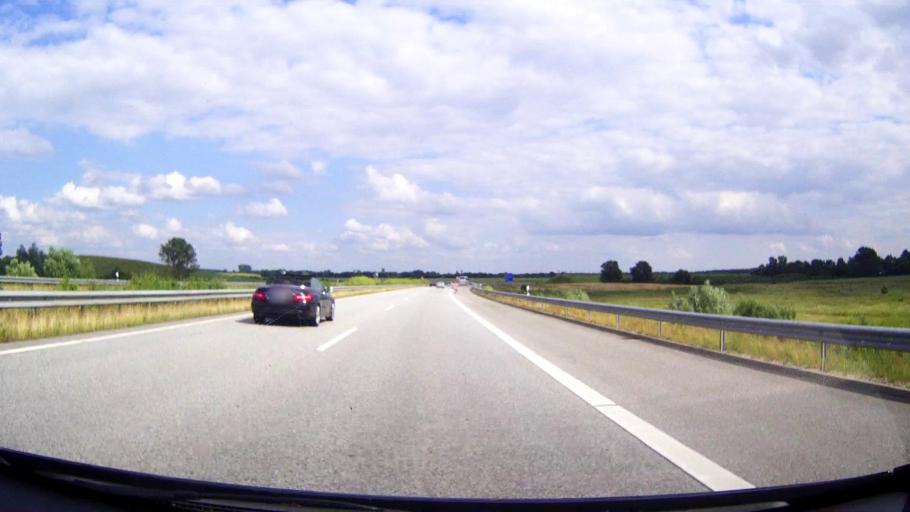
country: DE
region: Schleswig-Holstein
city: Monkhagen
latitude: 53.9092
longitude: 10.5583
